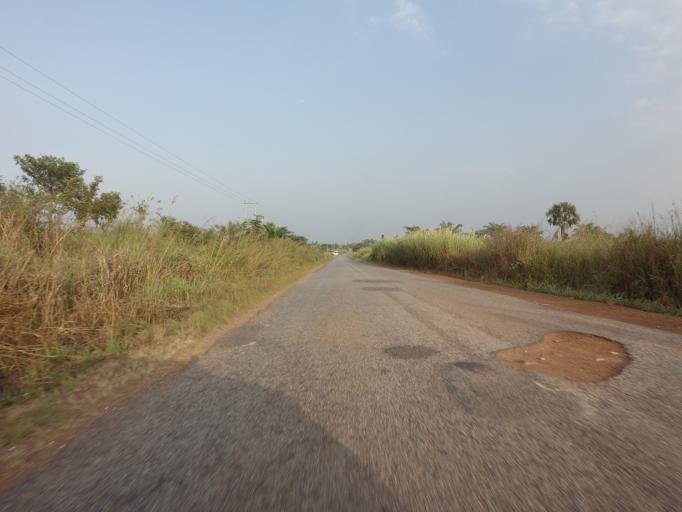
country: GH
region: Volta
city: Ho
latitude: 6.5753
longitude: 0.3255
